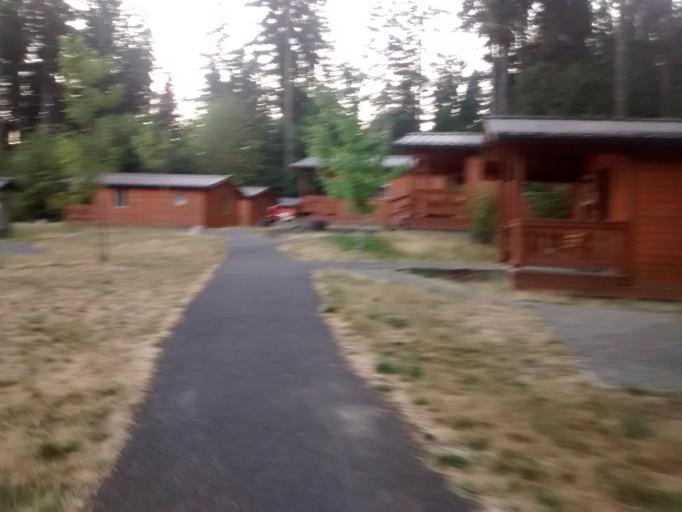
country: US
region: Oregon
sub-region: Columbia County
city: Vernonia
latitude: 45.7445
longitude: -123.1856
